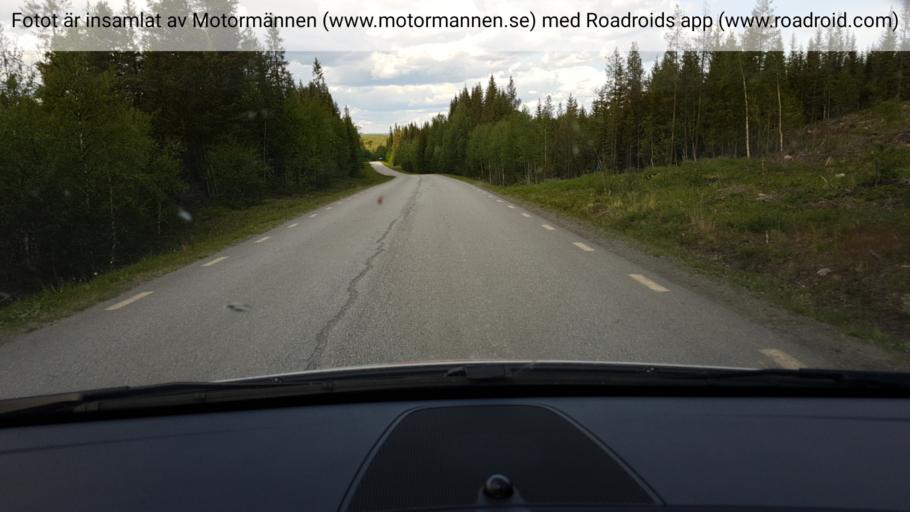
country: SE
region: Jaemtland
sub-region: Bergs Kommun
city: Hoverberg
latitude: 63.0387
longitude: 14.0174
